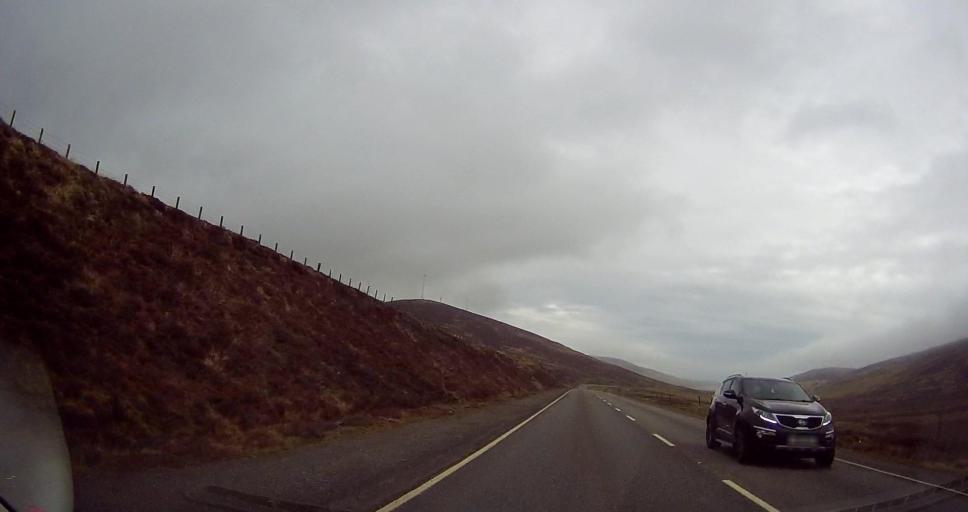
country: GB
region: Scotland
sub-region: Shetland Islands
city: Lerwick
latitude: 60.1516
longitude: -1.2371
